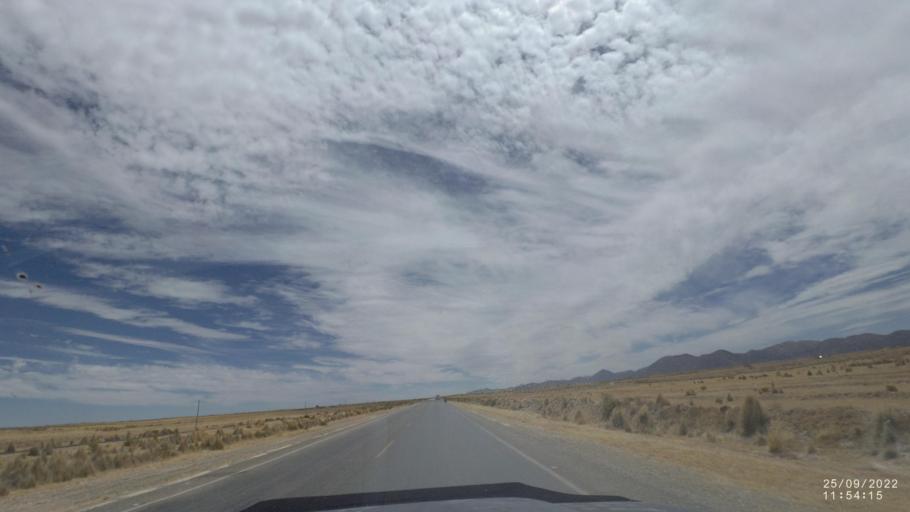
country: BO
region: Oruro
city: Challapata
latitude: -18.8765
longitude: -66.7925
